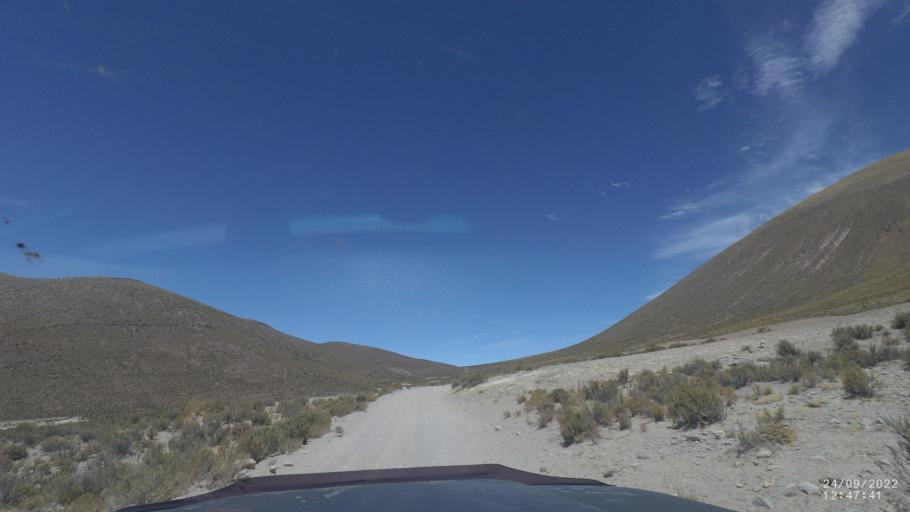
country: BO
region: Potosi
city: Colchani
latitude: -19.8114
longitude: -67.5676
